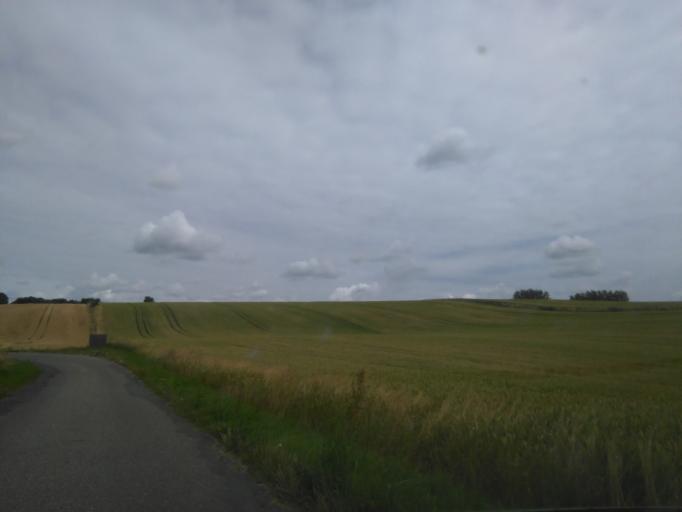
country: DK
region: Central Jutland
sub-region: Arhus Kommune
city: Solbjerg
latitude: 56.0016
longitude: 10.0578
